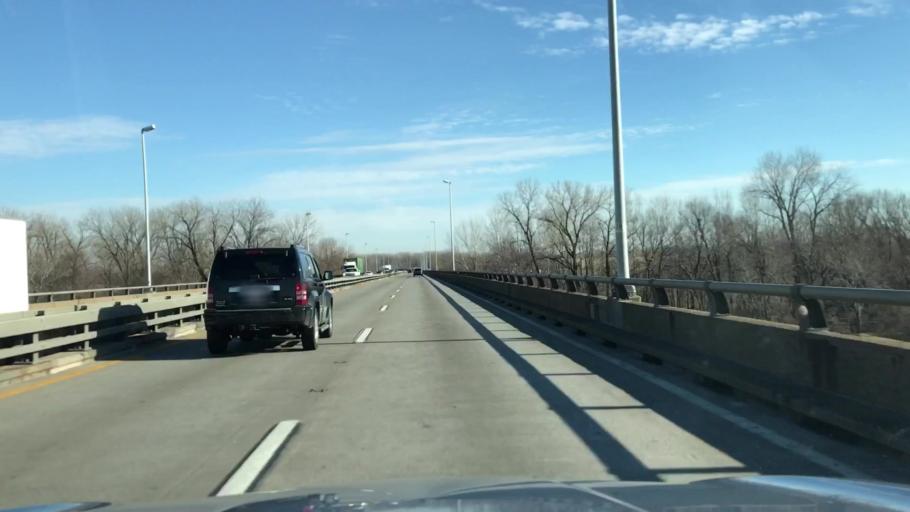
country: US
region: Missouri
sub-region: Saint Louis County
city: Glasgow Village
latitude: 38.7636
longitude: -90.1695
